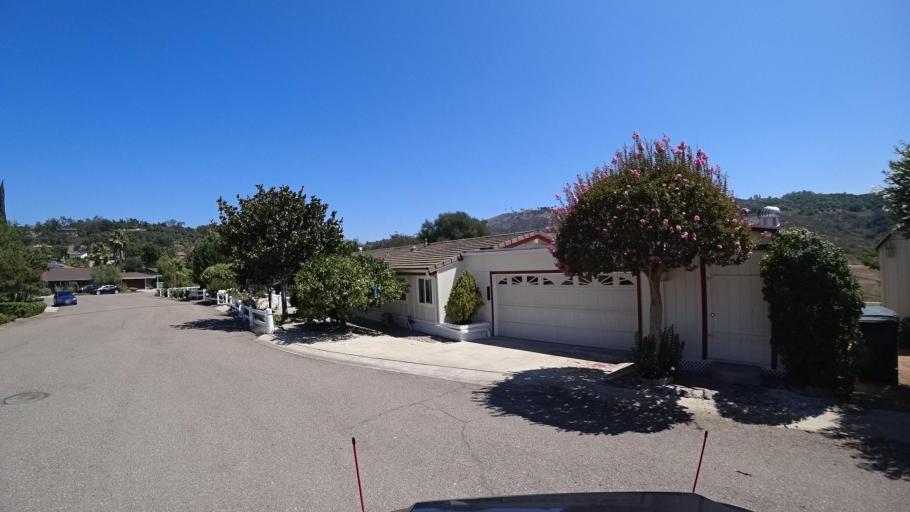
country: US
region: California
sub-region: San Diego County
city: Bonsall
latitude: 33.3353
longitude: -117.1861
